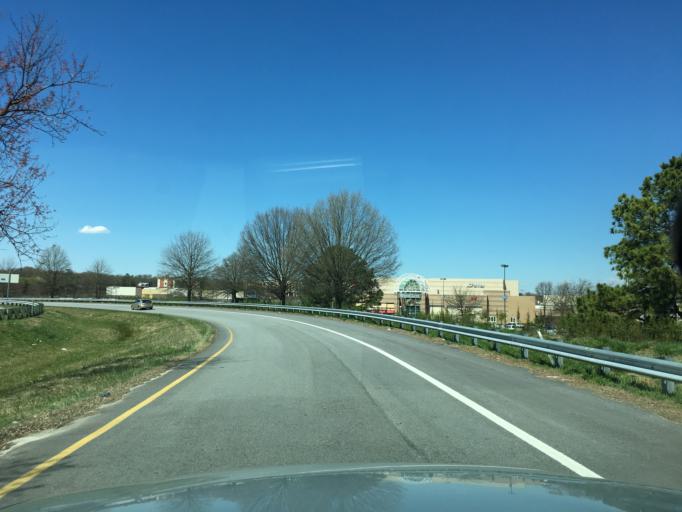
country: US
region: South Carolina
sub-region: Spartanburg County
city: Arcadia
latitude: 34.9372
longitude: -81.9947
